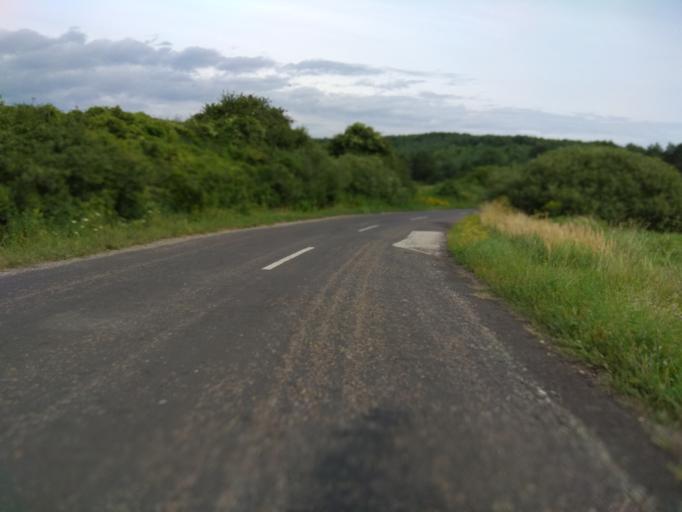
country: HU
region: Heves
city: Tarnalelesz
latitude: 48.0405
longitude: 20.2501
